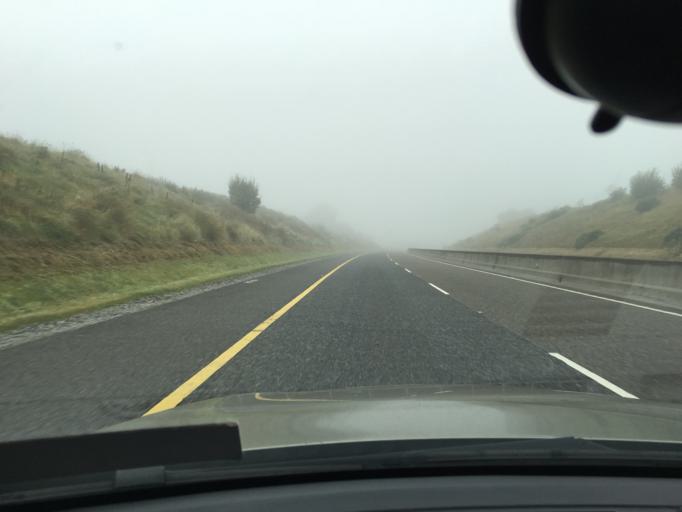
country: IE
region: Leinster
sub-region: Uibh Fhaili
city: Clara
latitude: 53.3860
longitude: -7.5959
